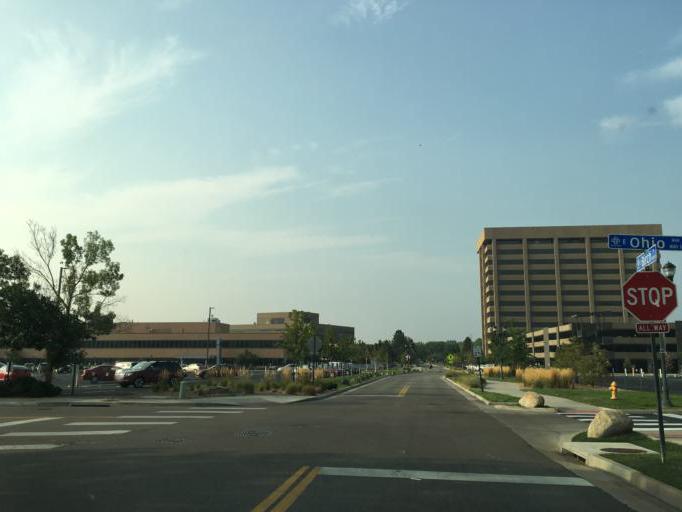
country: US
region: Colorado
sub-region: Arapahoe County
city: Glendale
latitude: 39.7019
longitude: -104.9363
